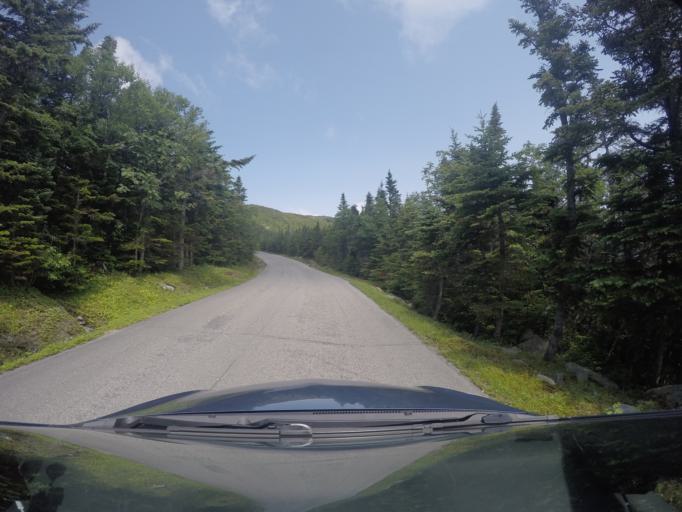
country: US
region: New Hampshire
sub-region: Coos County
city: Gorham
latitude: 44.2924
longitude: -71.2750
